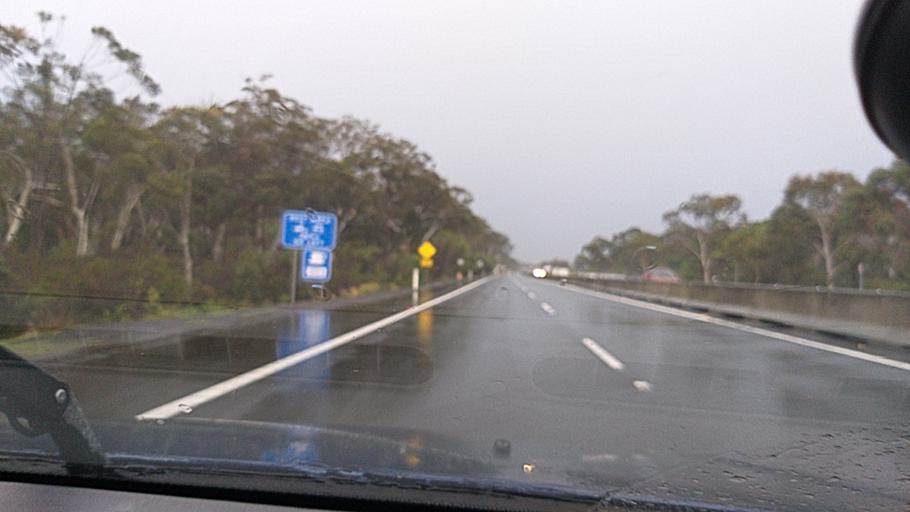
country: AU
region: New South Wales
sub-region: Wollondilly
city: Douglas Park
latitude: -34.2855
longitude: 150.7190
